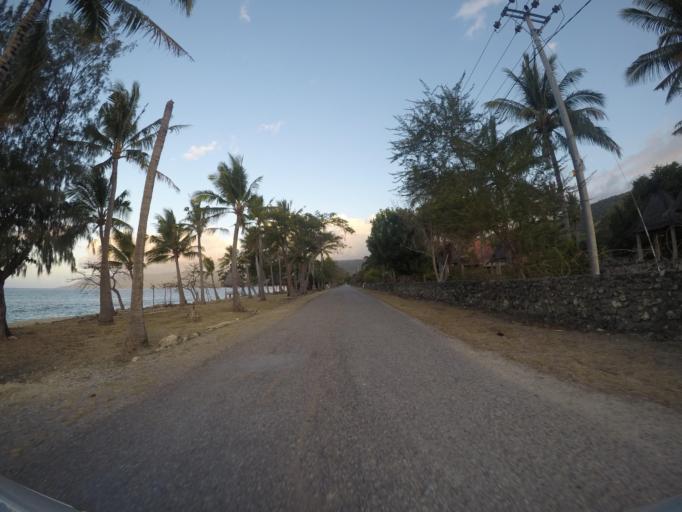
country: TL
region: Lautem
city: Lospalos
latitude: -8.3558
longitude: 127.0568
